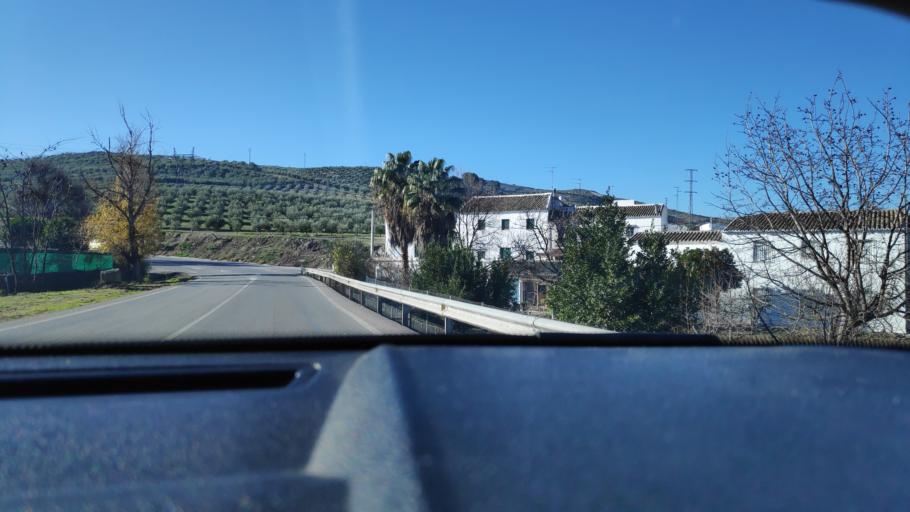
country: ES
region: Andalusia
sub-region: Province of Cordoba
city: Baena
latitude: 37.6110
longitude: -4.3225
